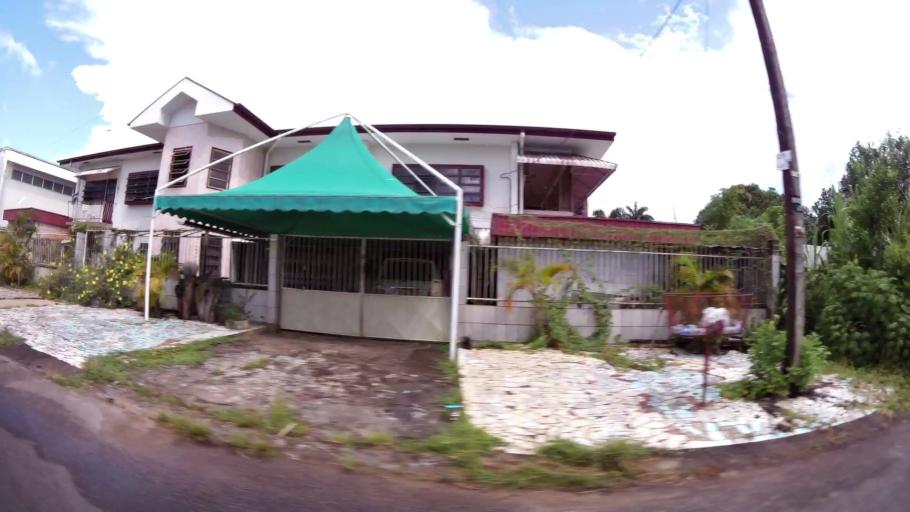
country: SR
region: Paramaribo
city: Paramaribo
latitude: 5.8374
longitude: -55.1252
